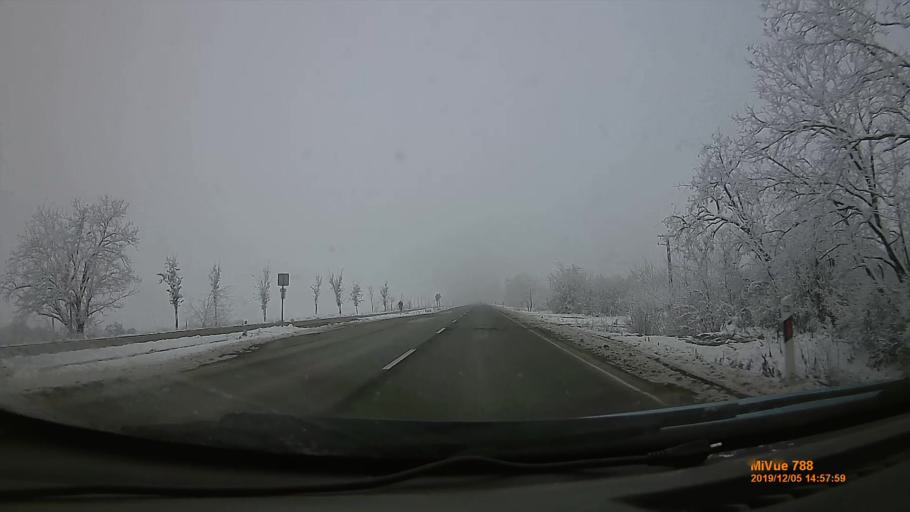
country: HU
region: Szabolcs-Szatmar-Bereg
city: Nyirtelek
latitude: 48.0442
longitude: 21.5781
